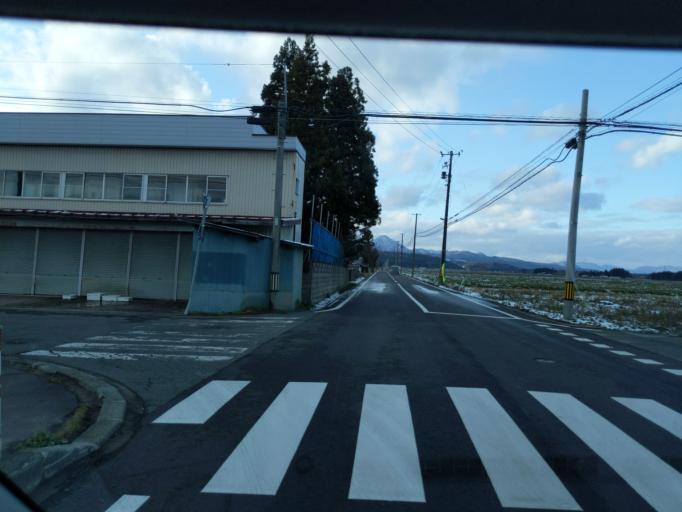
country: JP
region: Iwate
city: Kitakami
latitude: 39.2055
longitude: 141.0471
